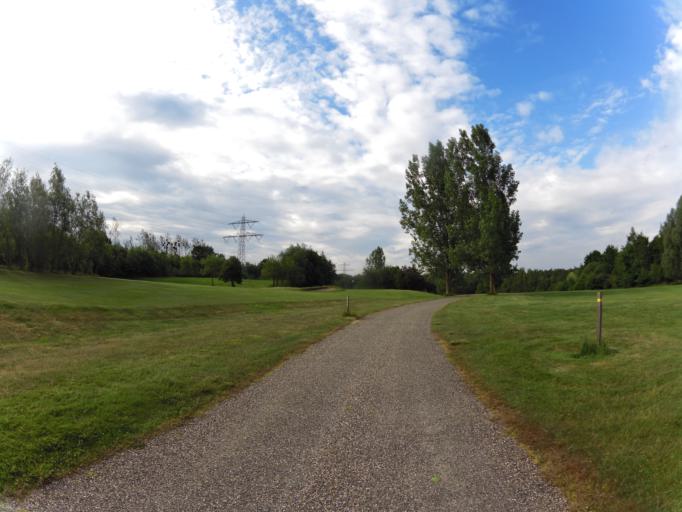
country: NL
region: Limburg
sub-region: Gemeente Brunssum
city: Brunssum
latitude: 50.9399
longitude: 6.0155
